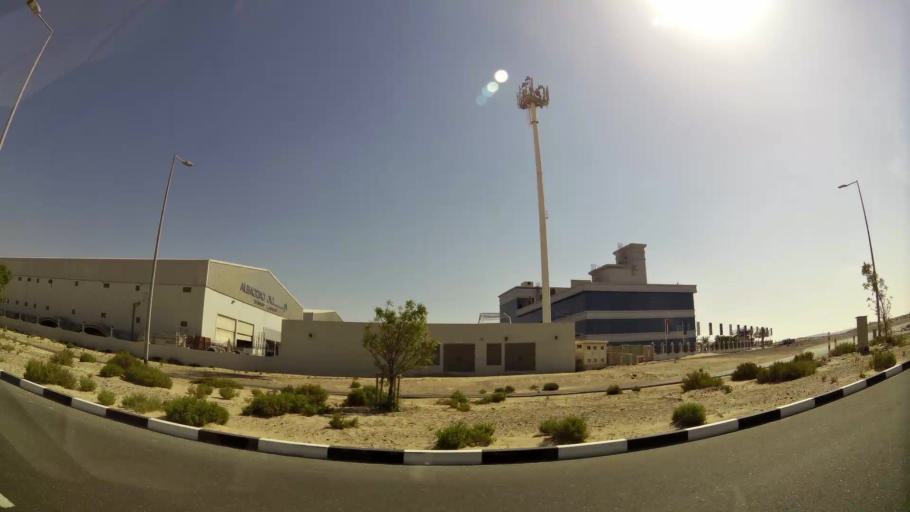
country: AE
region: Dubai
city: Dubai
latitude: 24.9264
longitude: 55.0597
